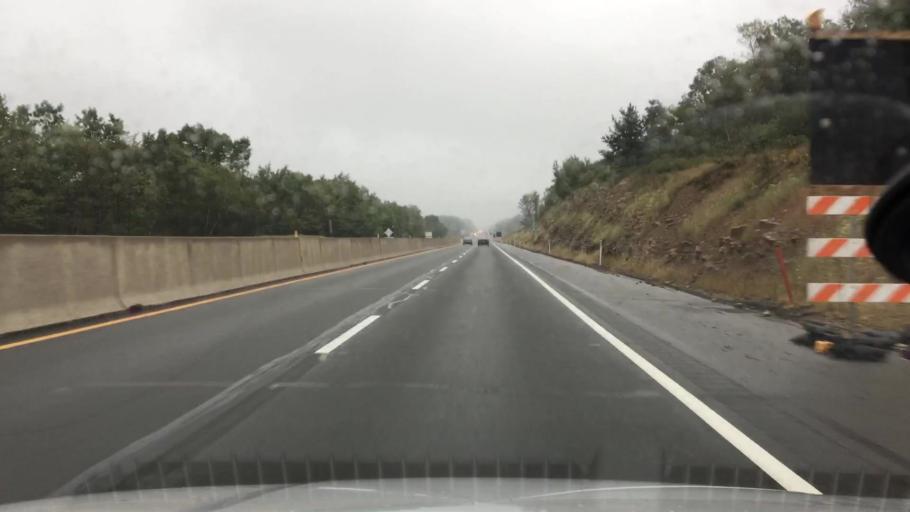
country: US
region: Pennsylvania
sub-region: Luzerne County
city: White Haven
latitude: 41.1353
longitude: -75.7773
